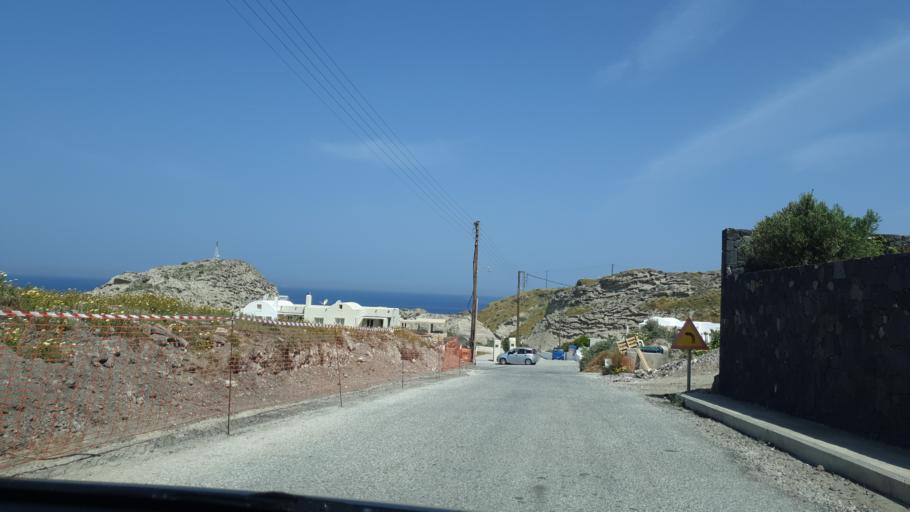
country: GR
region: South Aegean
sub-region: Nomos Kykladon
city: Oia
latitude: 36.4641
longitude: 25.3705
